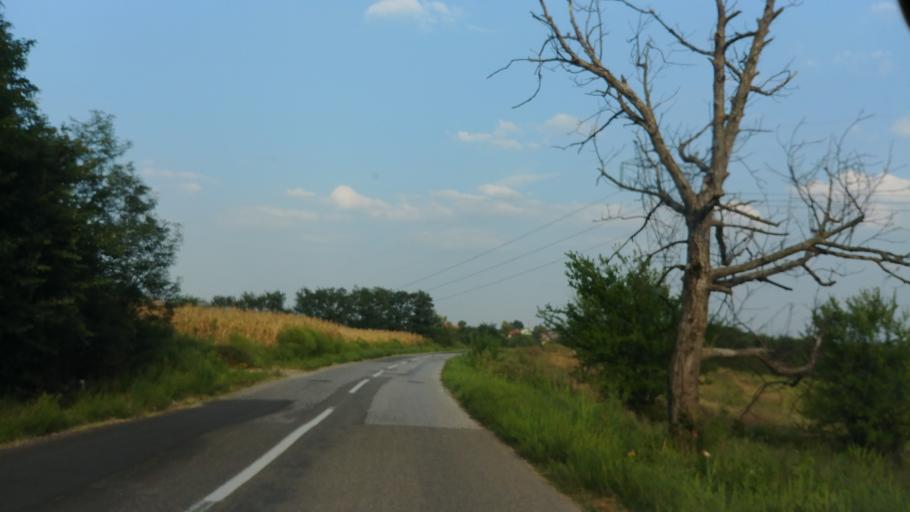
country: BA
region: Republika Srpska
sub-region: Opstina Ugljevik
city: Ugljevik
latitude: 44.7075
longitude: 18.9777
